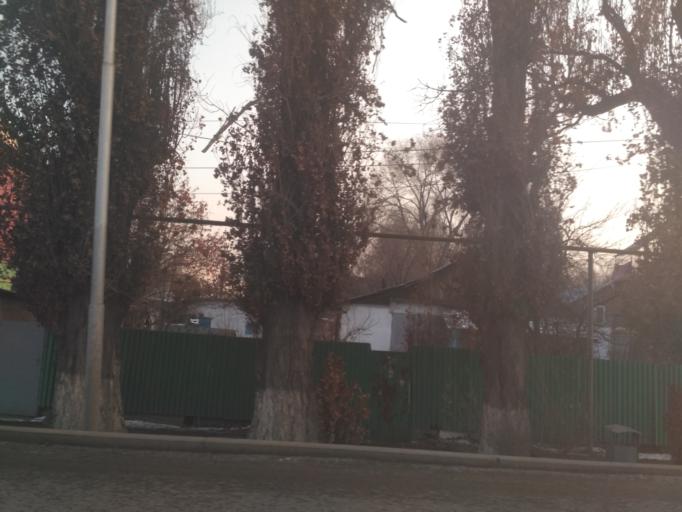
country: KZ
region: Almaty Qalasy
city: Almaty
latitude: 43.2492
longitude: 76.8460
